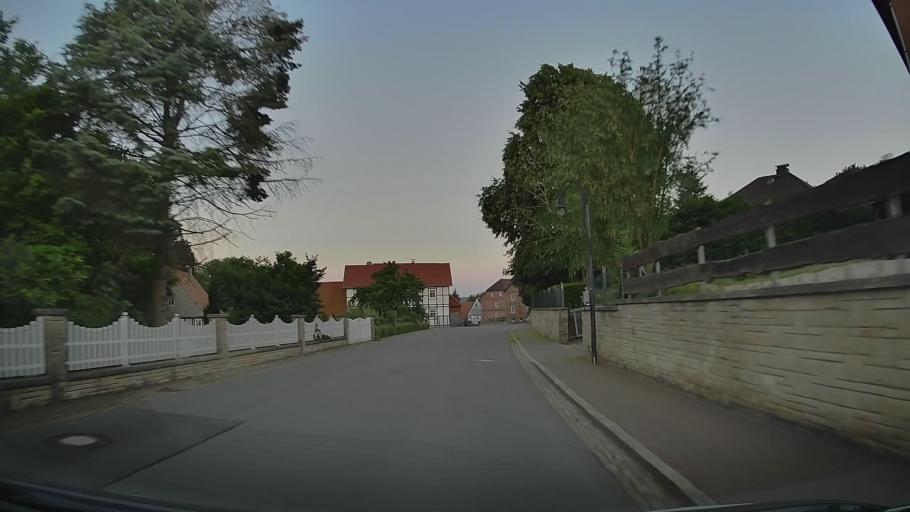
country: DE
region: Lower Saxony
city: Aerzen
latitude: 52.0165
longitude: 9.3096
